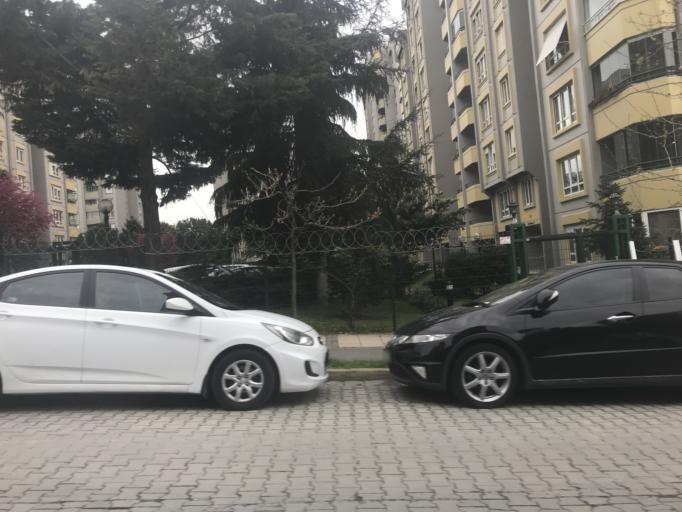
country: TR
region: Istanbul
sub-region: Atasehir
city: Atasehir
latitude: 40.9920
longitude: 29.1297
